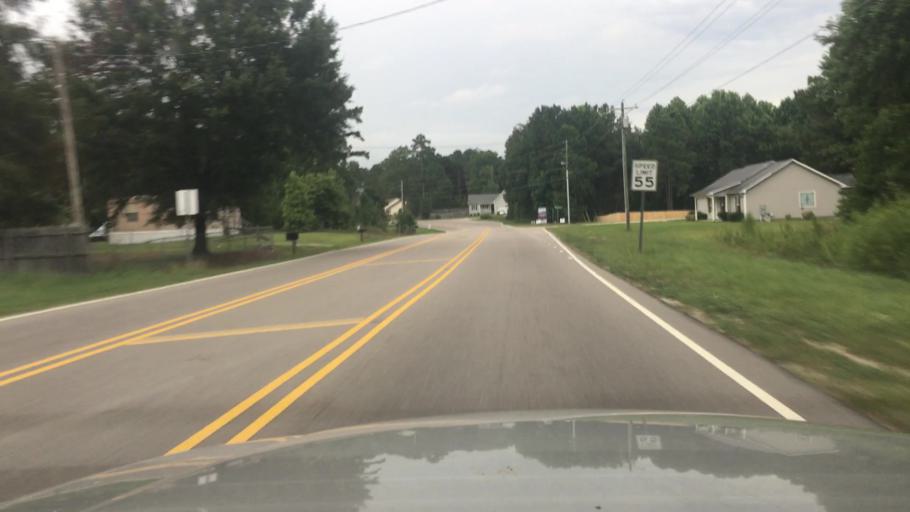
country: US
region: North Carolina
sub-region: Hoke County
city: Rockfish
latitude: 34.9660
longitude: -79.0528
